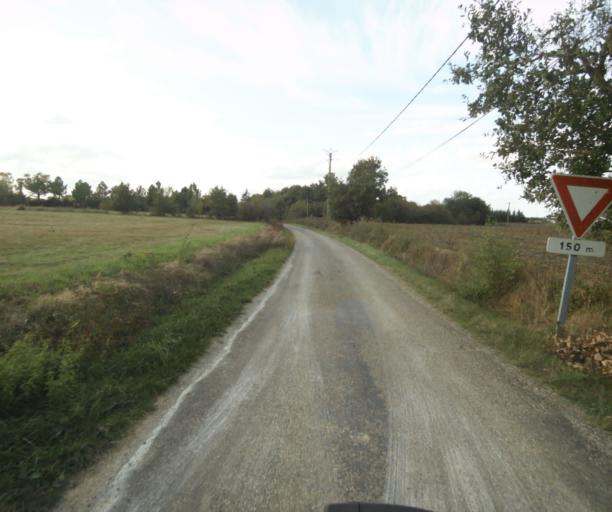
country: FR
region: Midi-Pyrenees
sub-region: Departement de la Haute-Garonne
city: Launac
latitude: 43.8131
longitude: 1.0979
